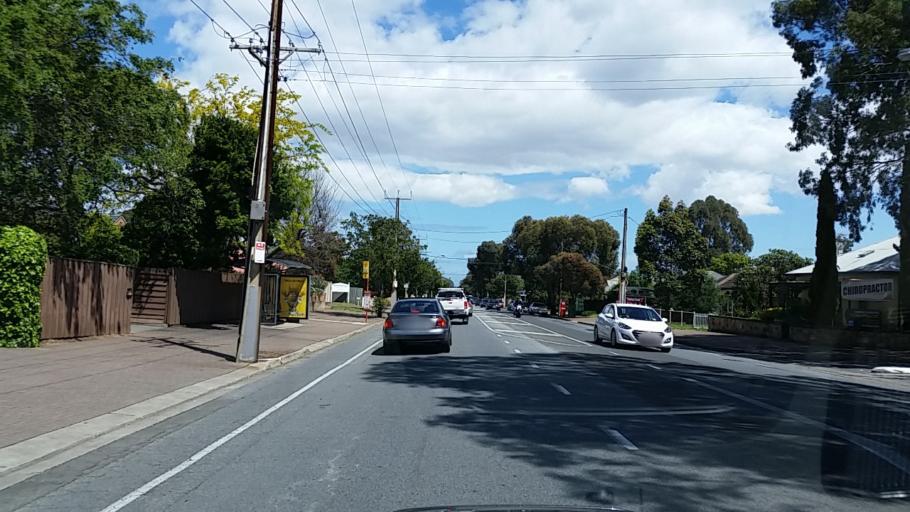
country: AU
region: South Australia
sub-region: Burnside
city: Wattle Park
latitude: -34.9134
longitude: 138.6692
